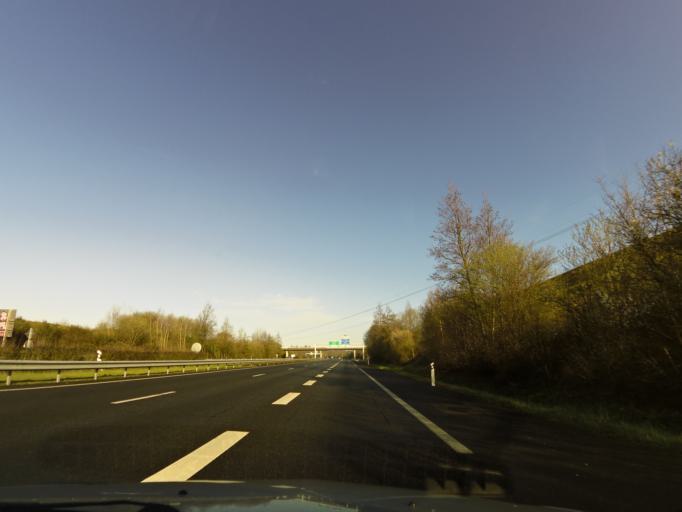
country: FR
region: Brittany
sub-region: Departement d'Ille-et-Vilaine
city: Fouillard
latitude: 48.1456
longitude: -1.5903
